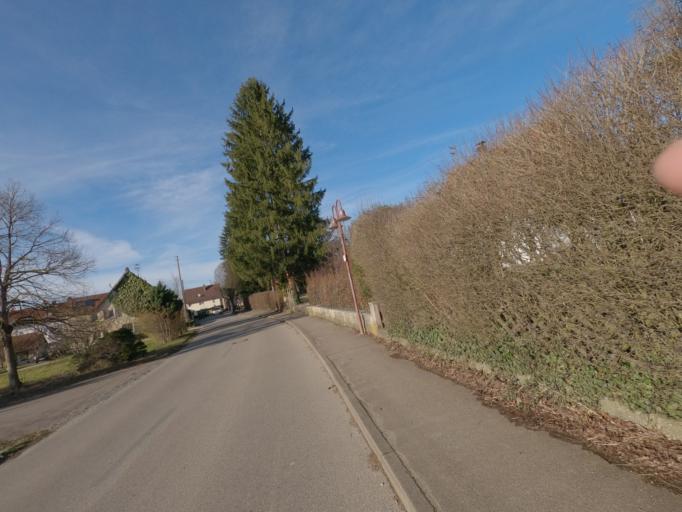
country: DE
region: Baden-Wuerttemberg
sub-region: Regierungsbezirk Stuttgart
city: Donzdorf
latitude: 48.7069
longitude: 9.7983
